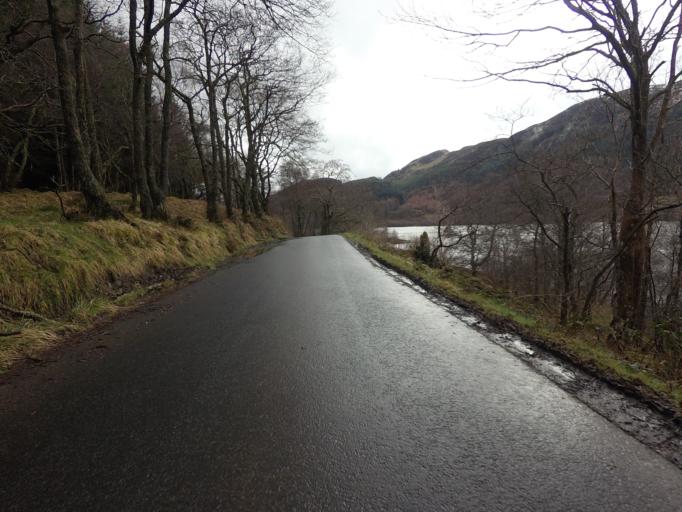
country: GB
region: Scotland
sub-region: West Dunbartonshire
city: Balloch
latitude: 56.2150
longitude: -4.5435
